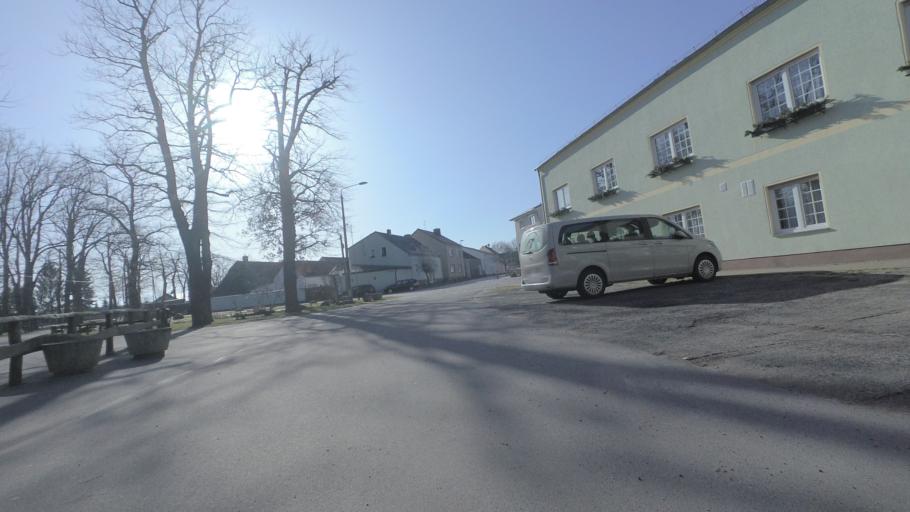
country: DE
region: Brandenburg
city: Luckenwalde
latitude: 52.0601
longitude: 13.1663
